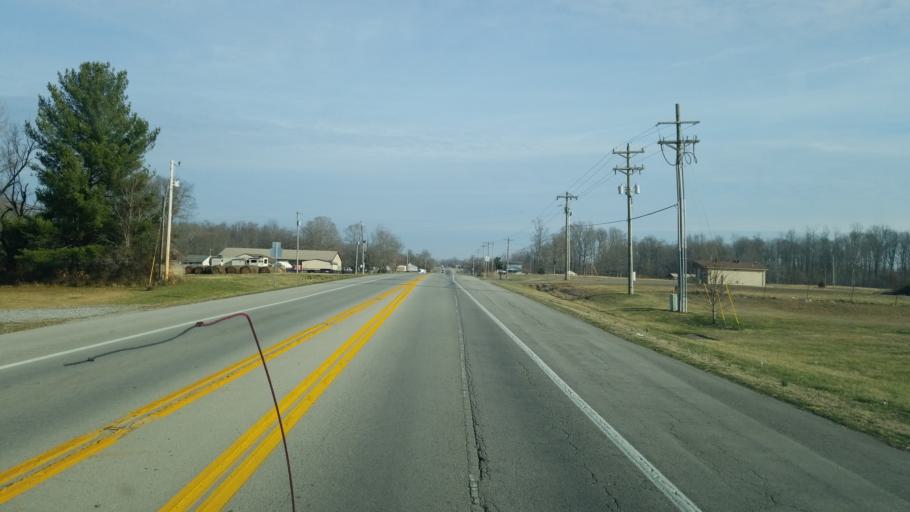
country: US
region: Kentucky
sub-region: Russell County
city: Russell Springs
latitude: 37.0895
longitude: -85.0655
